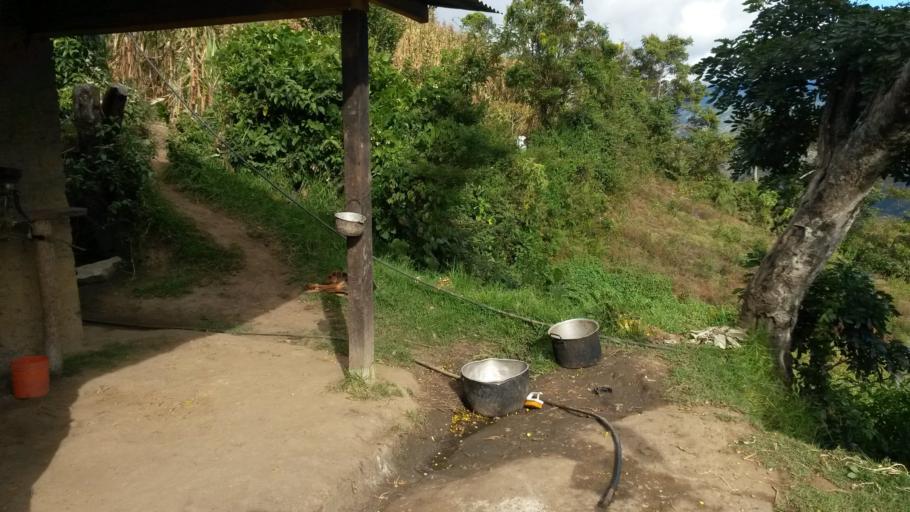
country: CO
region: Cauca
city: Almaguer
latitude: 1.8771
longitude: -76.8227
